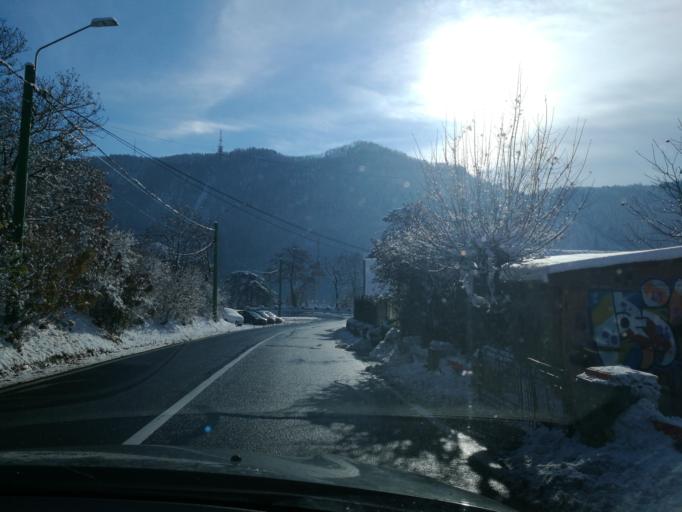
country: RO
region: Brasov
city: Brasov
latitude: 45.6427
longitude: 25.5835
